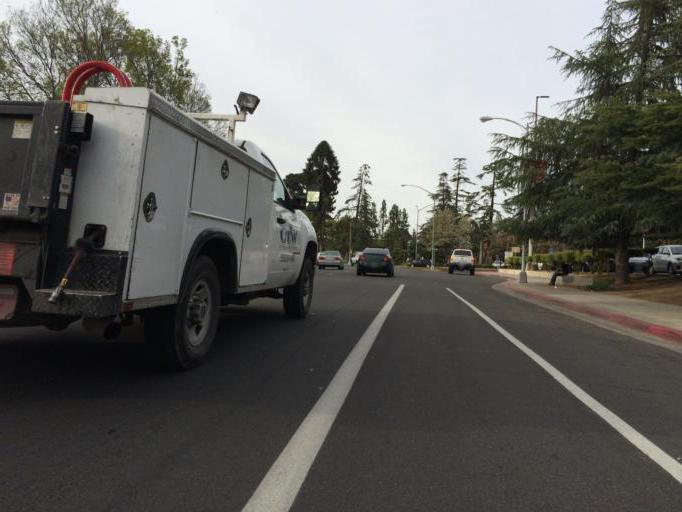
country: US
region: California
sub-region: Fresno County
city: Fresno
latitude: 36.7657
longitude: -119.7990
